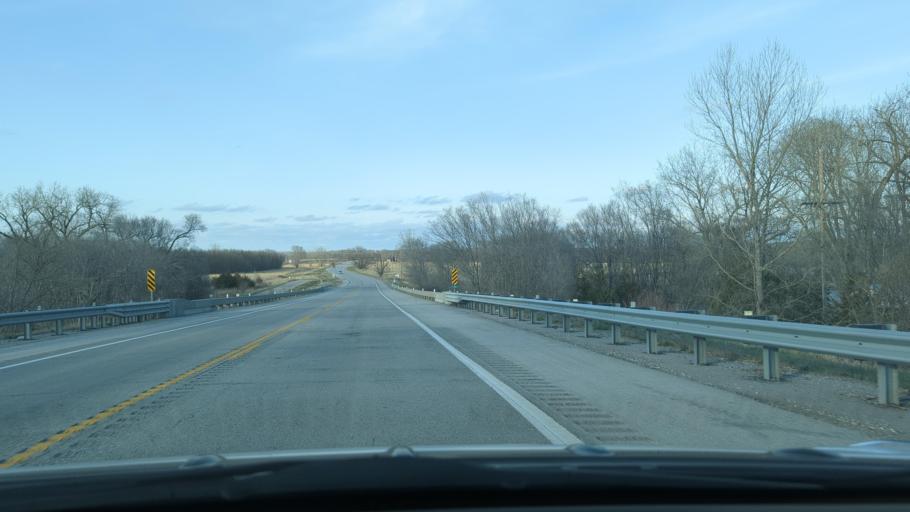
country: US
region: Nebraska
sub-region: Saunders County
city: Ashland
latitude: 41.0510
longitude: -96.3393
